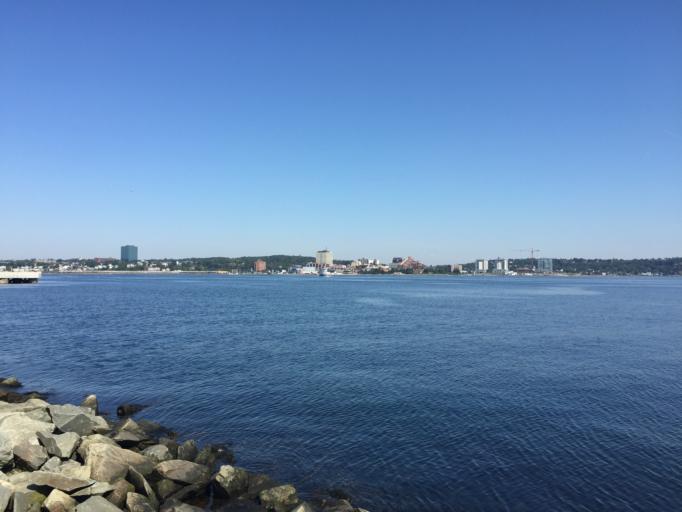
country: CA
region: Nova Scotia
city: Halifax
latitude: 44.6511
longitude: -63.5727
